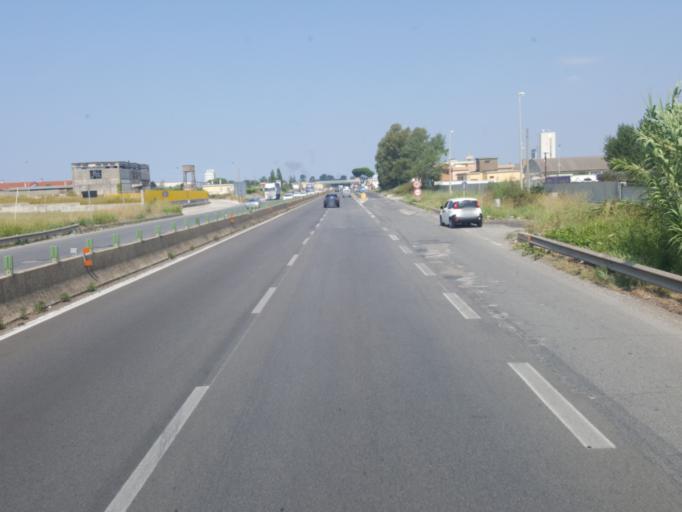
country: IT
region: Latium
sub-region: Provincia di Latina
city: Aprilia
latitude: 41.5733
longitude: 12.6616
